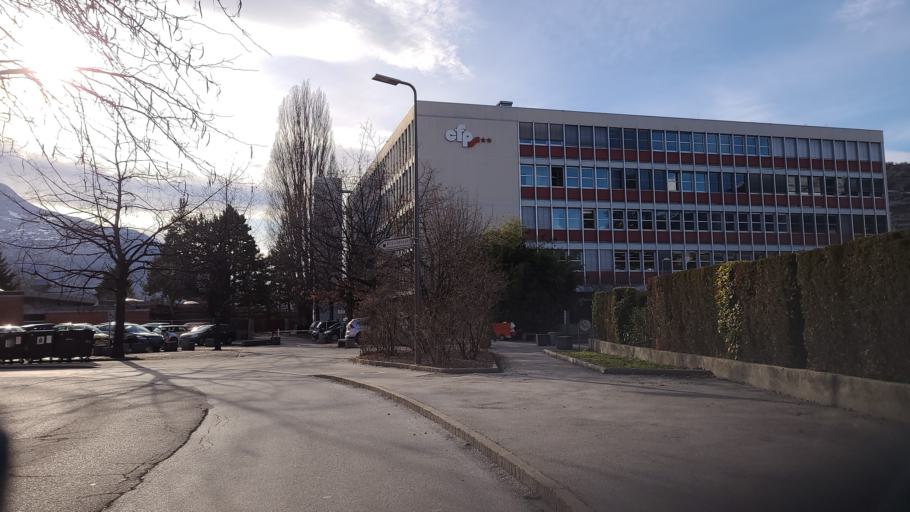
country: CH
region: Valais
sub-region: Sion District
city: Sitten
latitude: 46.2274
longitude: 7.3550
